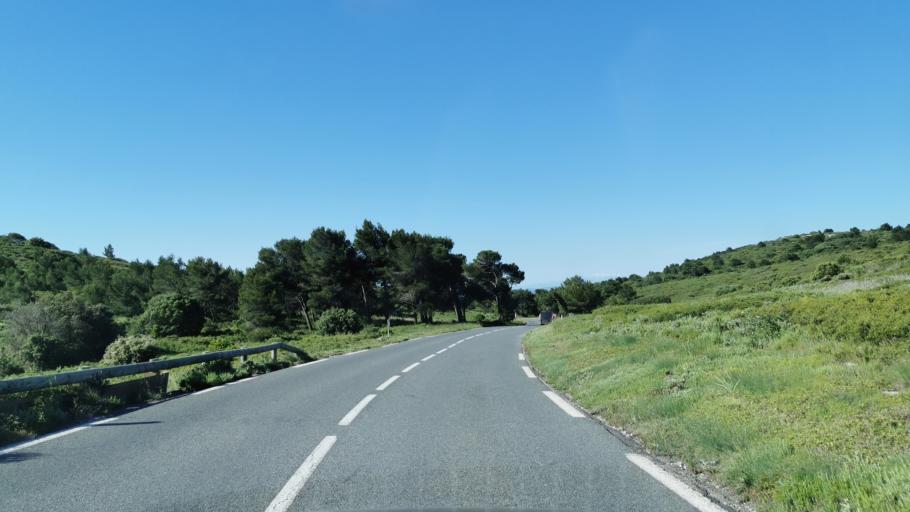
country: FR
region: Languedoc-Roussillon
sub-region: Departement de l'Aude
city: Armissan
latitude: 43.1704
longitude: 3.1346
